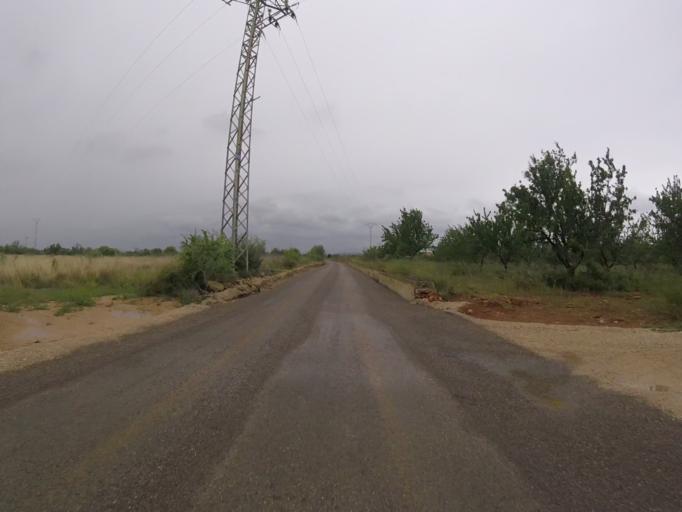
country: ES
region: Valencia
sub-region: Provincia de Castello
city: Alcoceber
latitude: 40.2354
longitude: 0.2569
